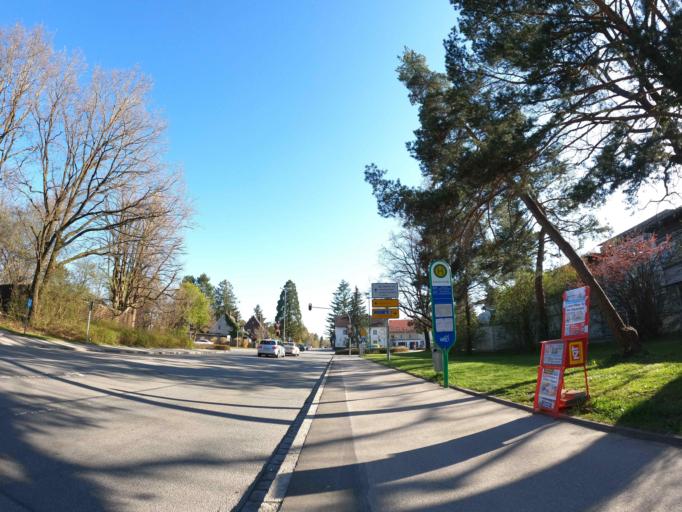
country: DE
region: Bavaria
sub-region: Upper Bavaria
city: Ottobrunn
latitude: 48.0636
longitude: 11.6532
